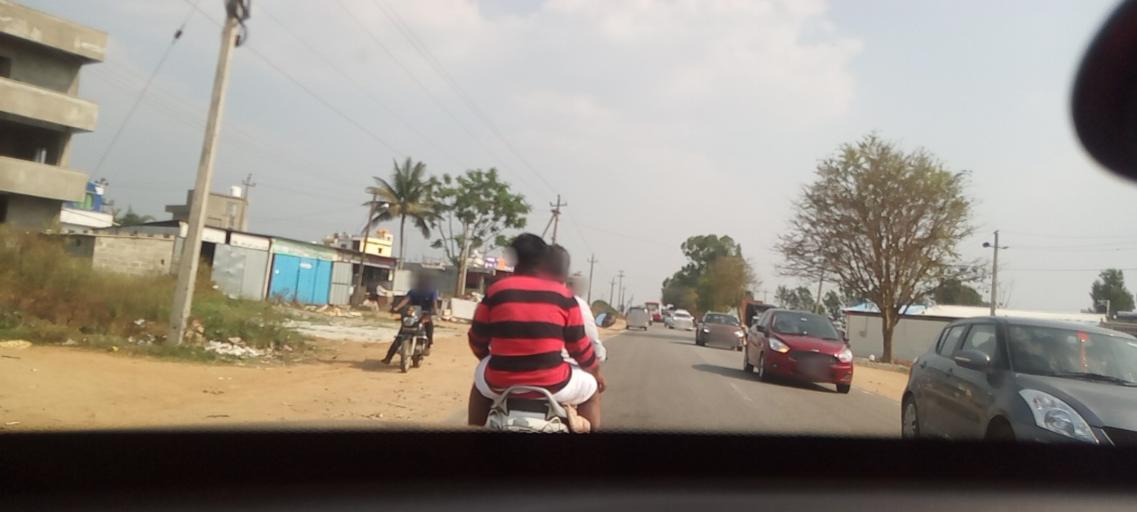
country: IN
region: Karnataka
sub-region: Hassan
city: Belur
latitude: 13.1256
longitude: 75.9944
